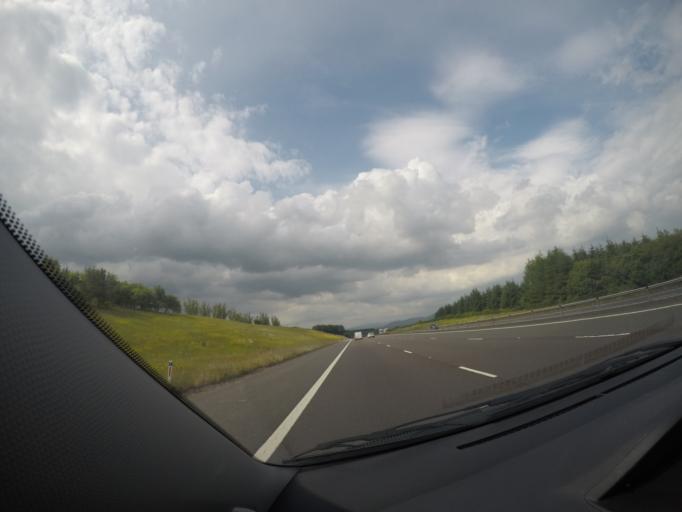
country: GB
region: Scotland
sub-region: Dumfries and Galloway
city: Lochmaben
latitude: 55.2212
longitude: -3.4132
